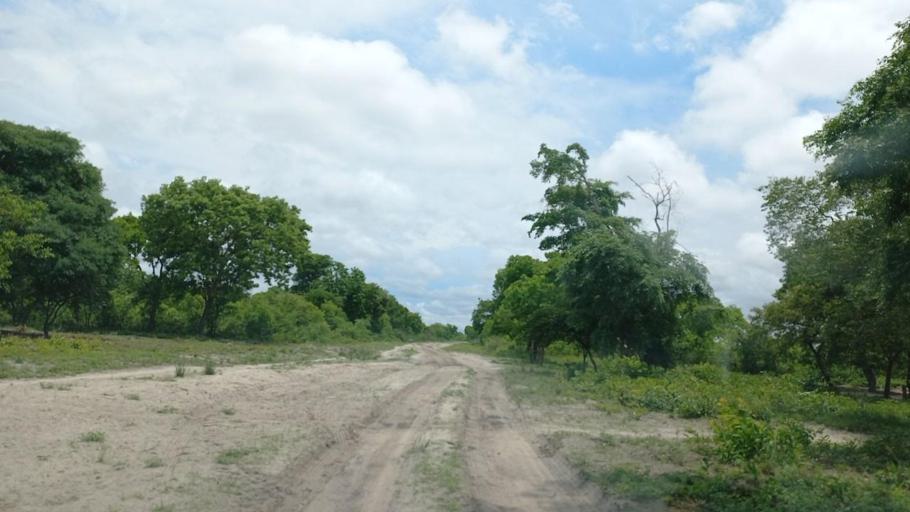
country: ZM
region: North-Western
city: Kabompo
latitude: -13.1773
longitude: 23.9463
